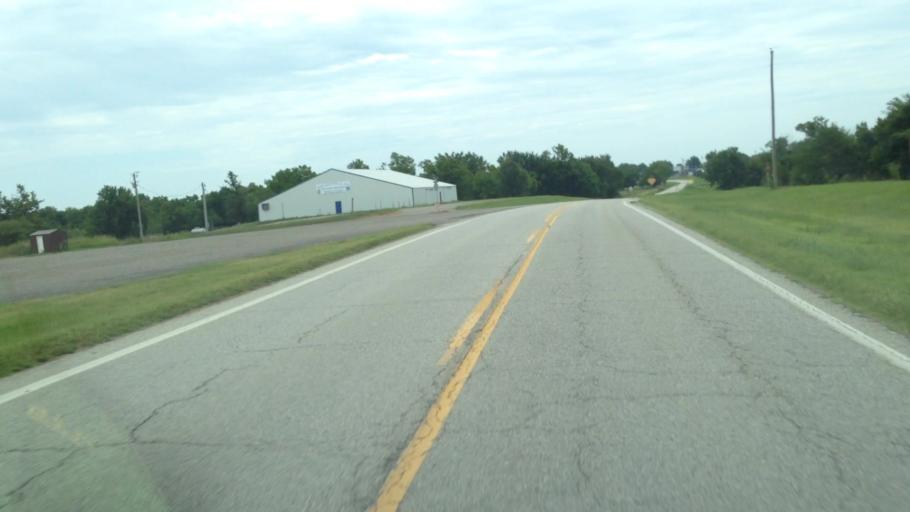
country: US
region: Kansas
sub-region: Labette County
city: Chetopa
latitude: 36.8649
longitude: -95.1084
